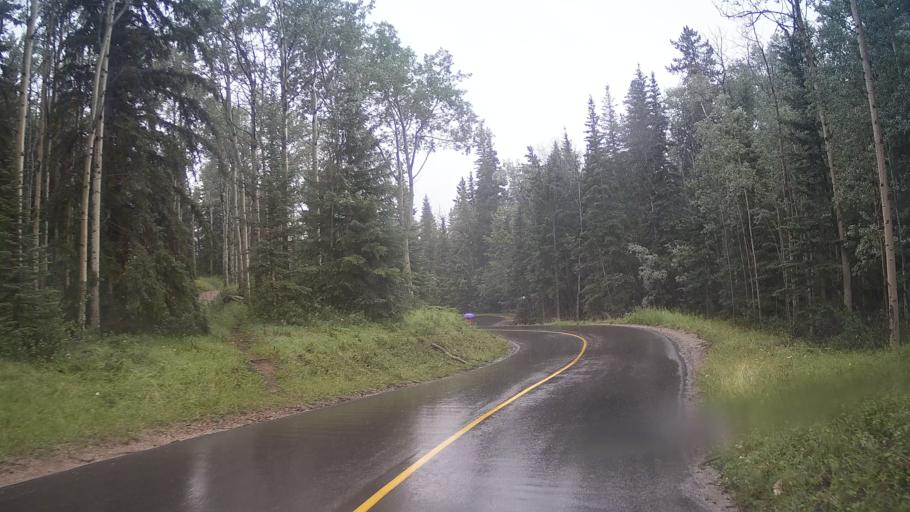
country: CA
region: Alberta
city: Jasper Park Lodge
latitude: 52.9119
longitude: -118.0924
